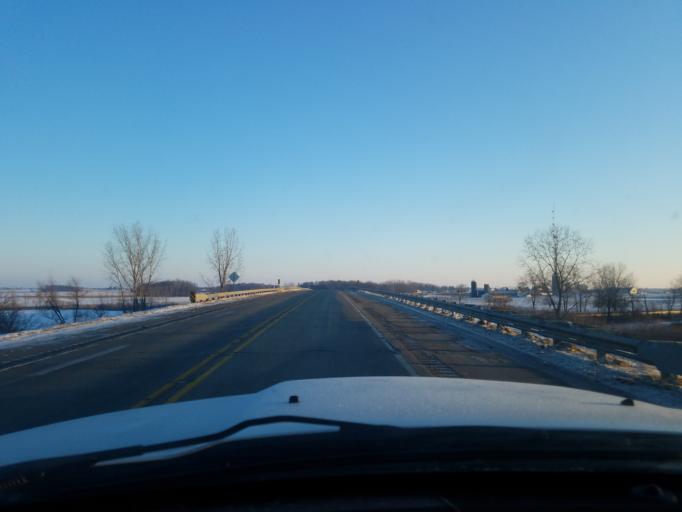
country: US
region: Indiana
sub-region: Marshall County
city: Bremen
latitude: 41.4537
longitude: -86.2022
